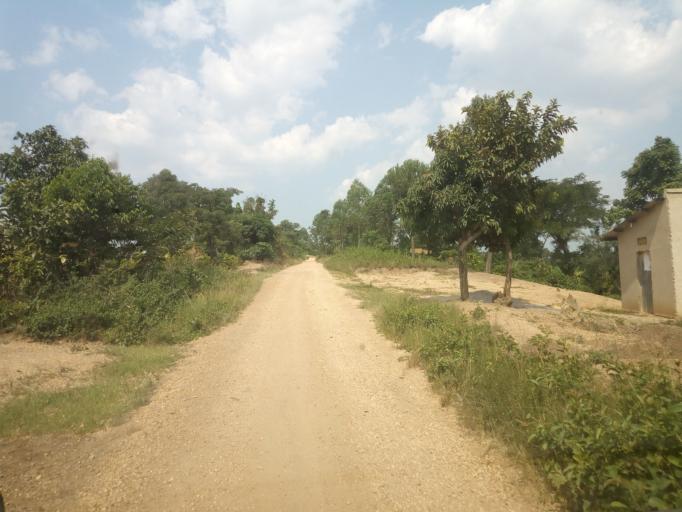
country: UG
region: Western Region
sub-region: Kanungu District
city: Ntungamo
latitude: -0.7891
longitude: 29.6555
